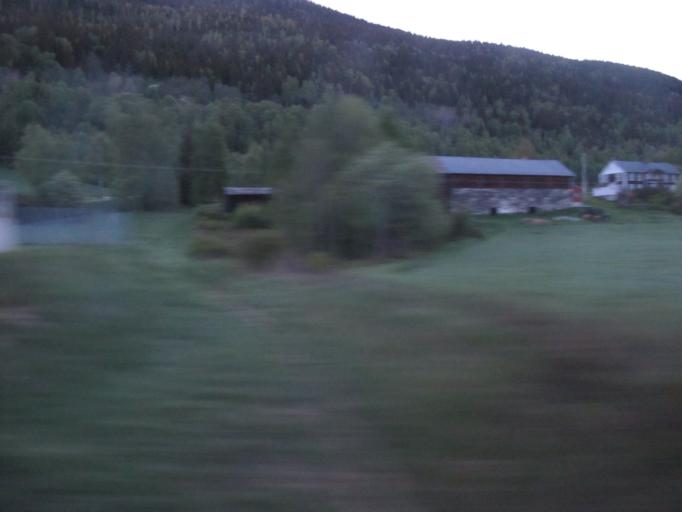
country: NO
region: Oppland
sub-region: Nord-Fron
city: Vinstra
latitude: 61.5809
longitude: 9.8423
